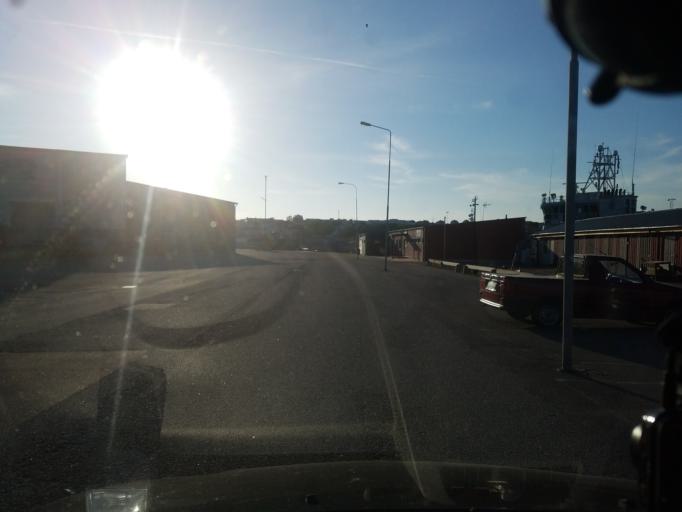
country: SE
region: Vaestra Goetaland
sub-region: Lysekils Kommun
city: Lysekil
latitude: 58.2735
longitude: 11.4507
